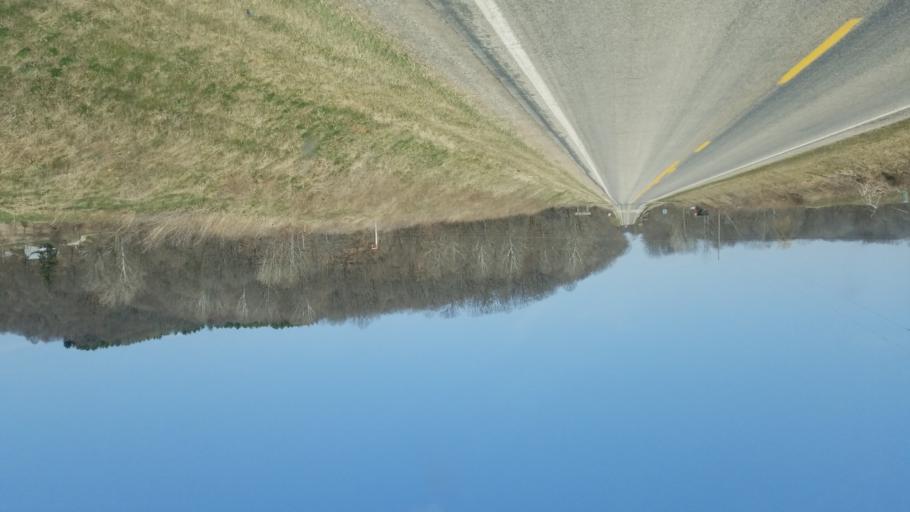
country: US
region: Ohio
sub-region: Ashland County
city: Loudonville
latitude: 40.7114
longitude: -82.1660
